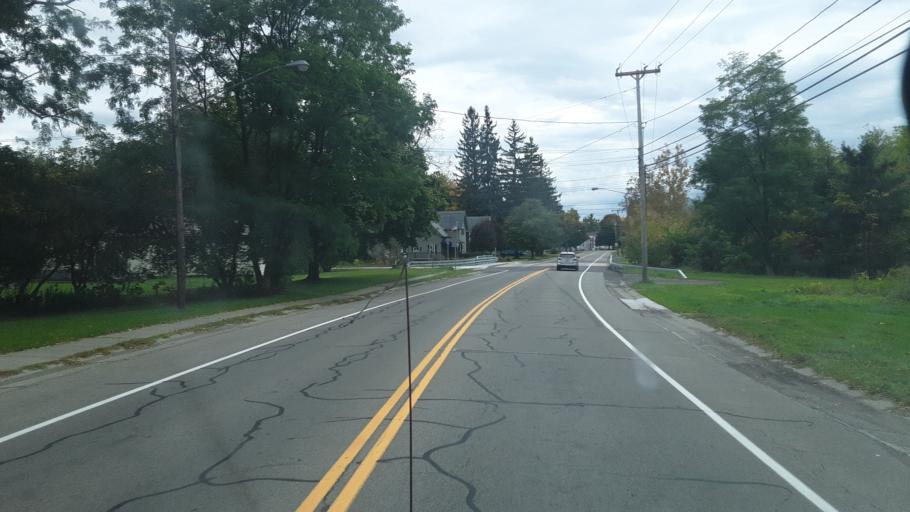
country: US
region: New York
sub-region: Allegany County
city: Belmont
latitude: 42.2245
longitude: -78.0276
